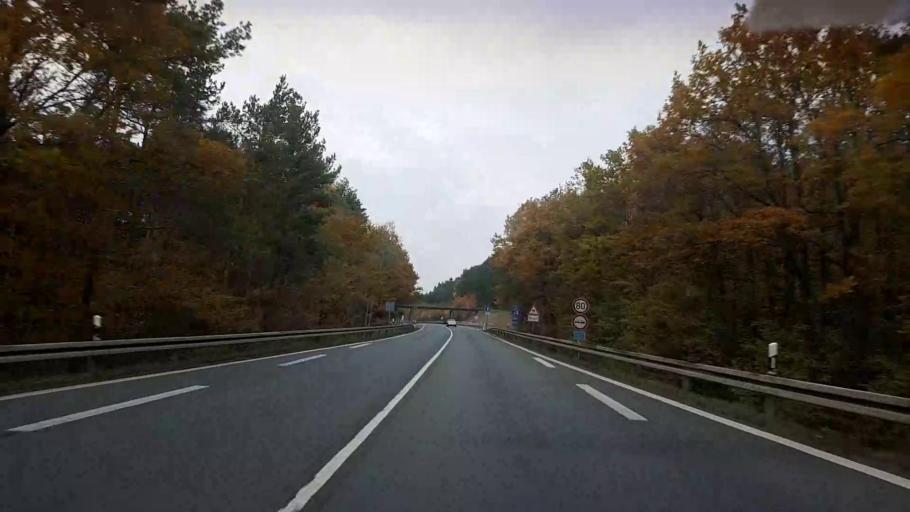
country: DE
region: Bavaria
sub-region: Regierungsbezirk Mittelfranken
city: Hochstadt an der Aisch
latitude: 49.7294
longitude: 10.8241
